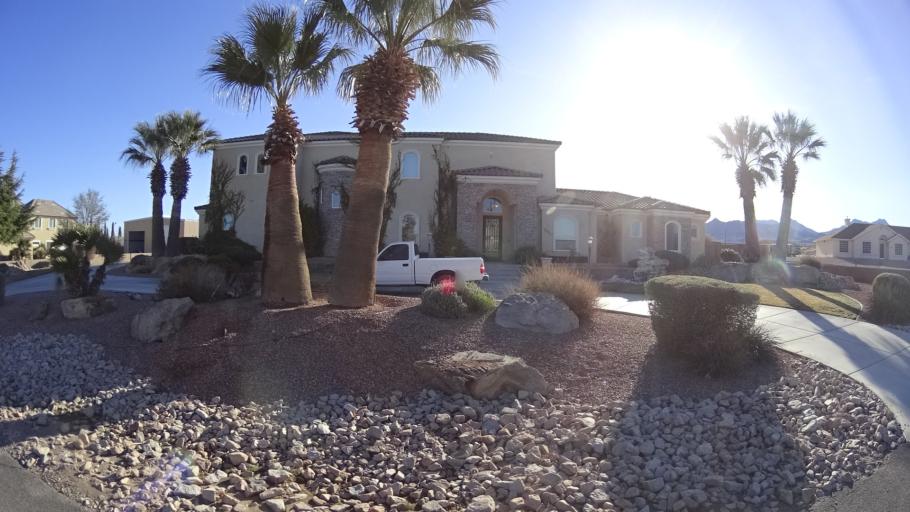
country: US
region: Arizona
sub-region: Mohave County
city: Kingman
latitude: 35.2086
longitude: -113.9960
